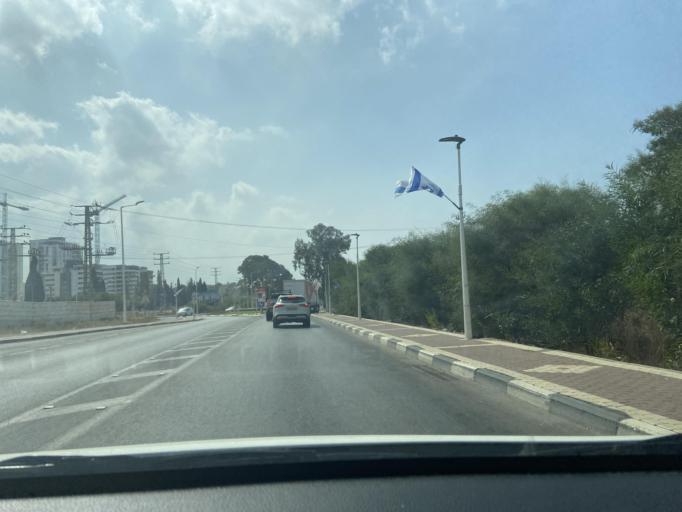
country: IL
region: Northern District
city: Nahariya
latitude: 33.0197
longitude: 35.1037
